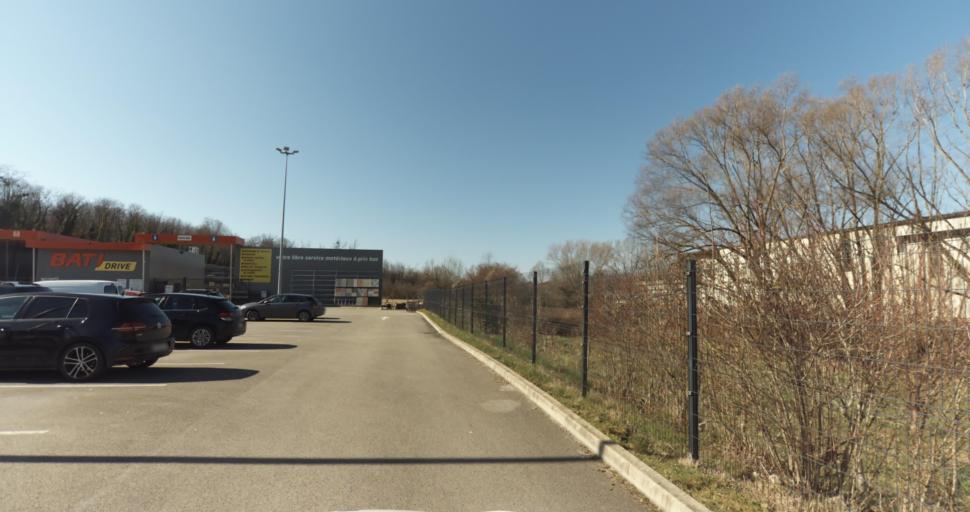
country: FR
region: Franche-Comte
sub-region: Departement du Jura
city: Montmorot
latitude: 46.6757
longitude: 5.5202
